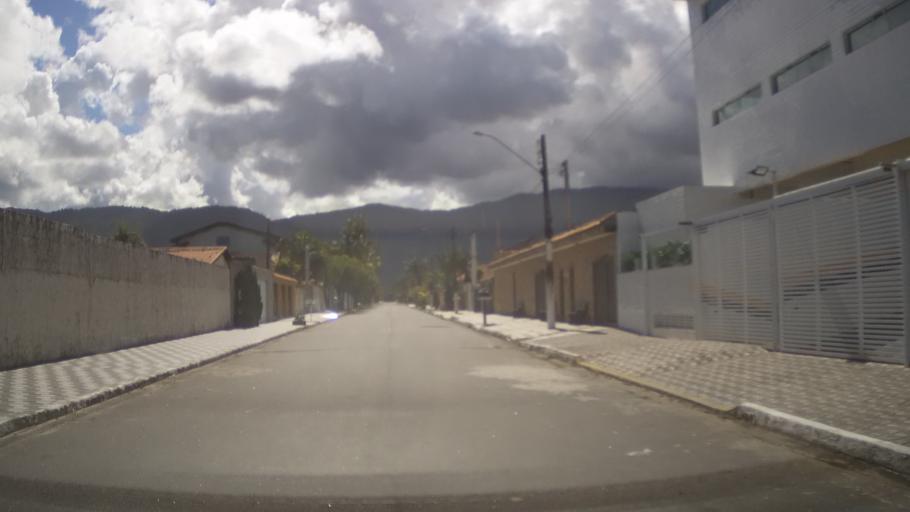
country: BR
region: Sao Paulo
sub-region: Mongagua
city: Mongagua
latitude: -24.0686
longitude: -46.5638
